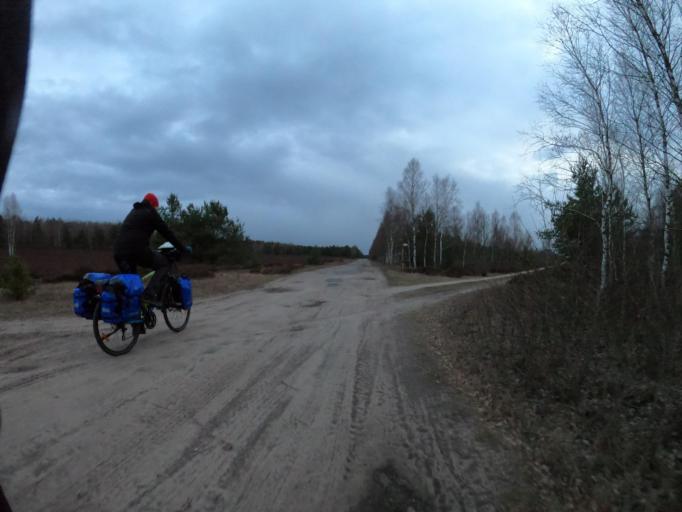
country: PL
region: West Pomeranian Voivodeship
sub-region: Powiat szczecinecki
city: Borne Sulinowo
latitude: 53.5265
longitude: 16.5702
